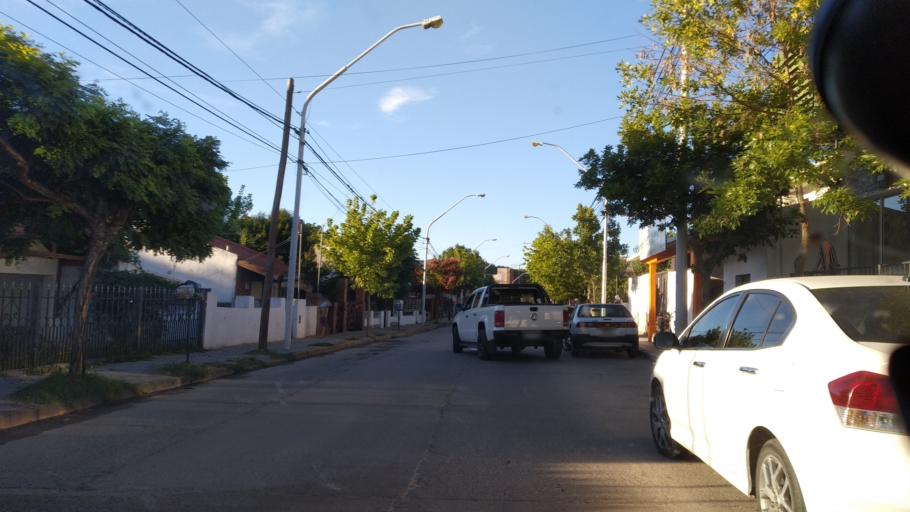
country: AR
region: Cordoba
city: Mina Clavero
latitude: -31.7176
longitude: -65.0057
